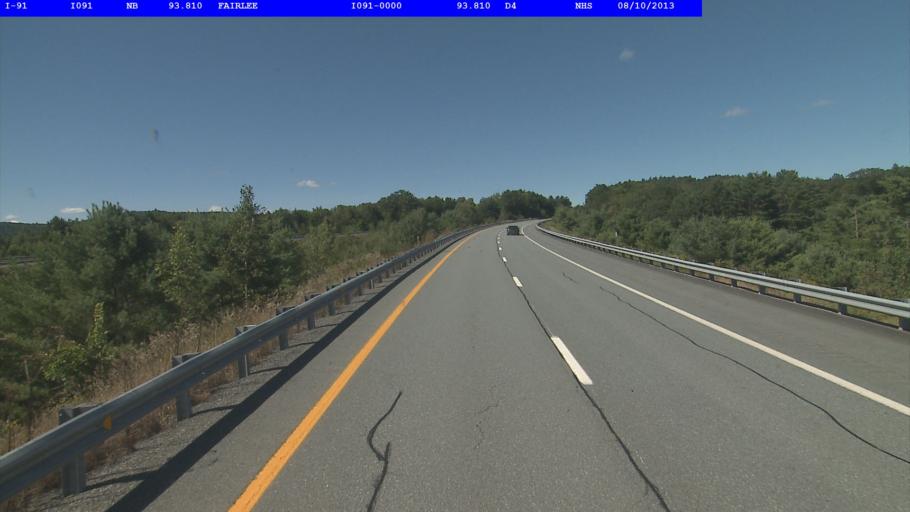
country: US
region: New Hampshire
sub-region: Grafton County
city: Orford
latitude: 43.9304
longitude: -72.1340
